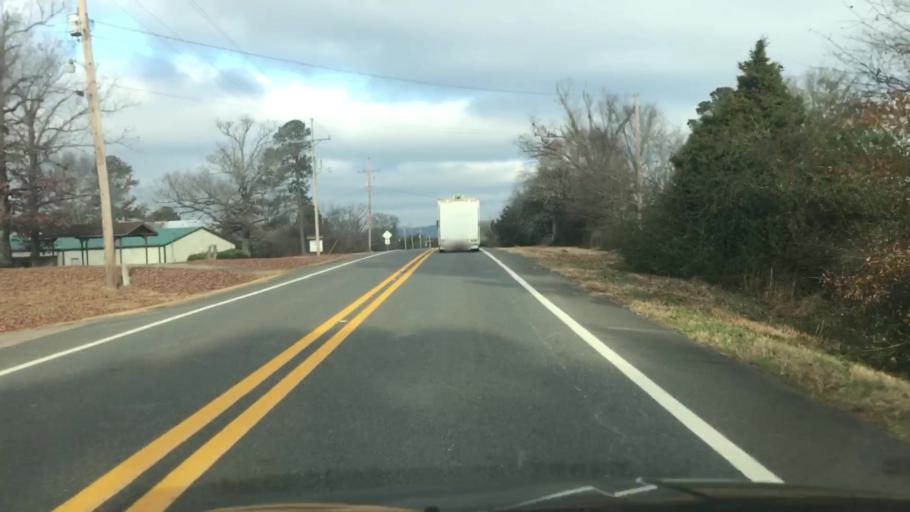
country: US
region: Arkansas
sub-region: Montgomery County
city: Mount Ida
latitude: 34.6262
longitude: -93.7310
